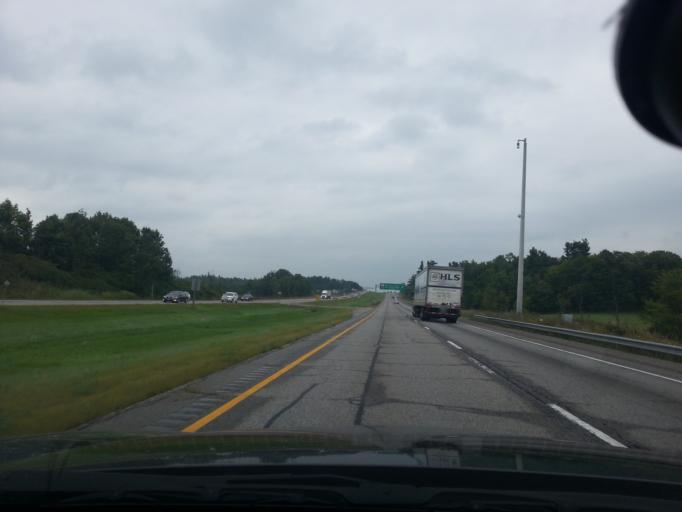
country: US
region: New York
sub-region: Jefferson County
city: Alexandria Bay
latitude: 44.3790
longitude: -75.9961
